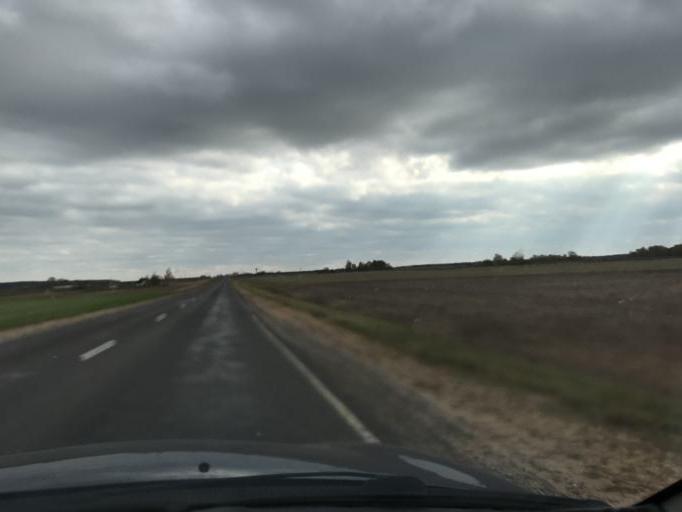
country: BY
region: Grodnenskaya
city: Lida
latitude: 53.8074
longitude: 25.1153
